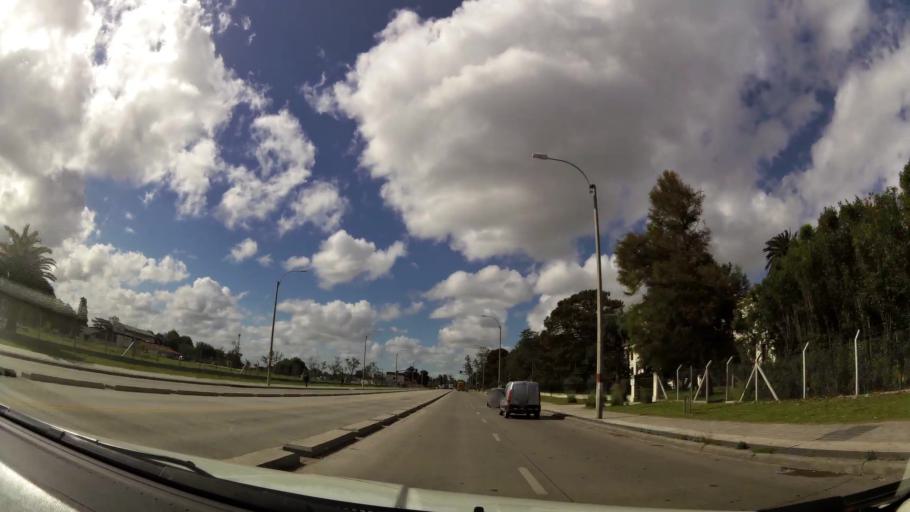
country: UY
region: Montevideo
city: Montevideo
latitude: -34.8376
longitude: -56.2217
